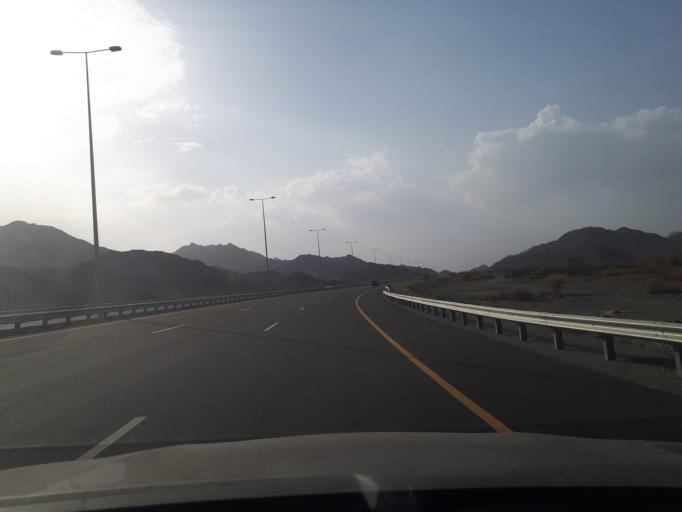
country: OM
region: Ash Sharqiyah
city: Ibra'
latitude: 22.8514
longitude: 58.3163
